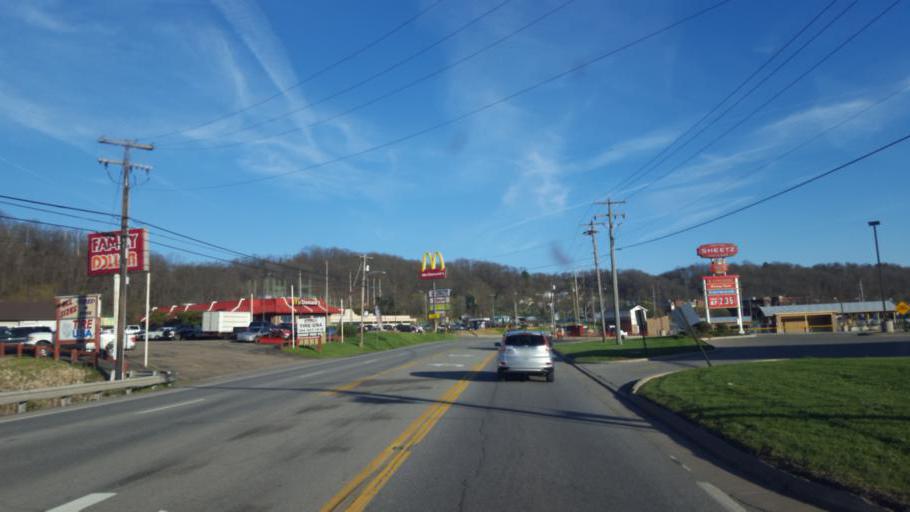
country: US
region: West Virginia
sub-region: Brooke County
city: Follansbee
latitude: 40.3389
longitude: -80.5978
